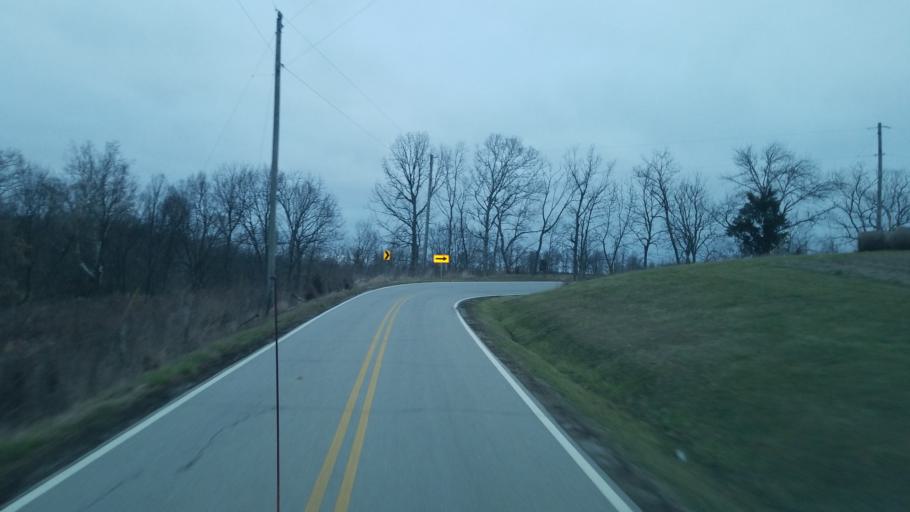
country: US
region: Kentucky
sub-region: Mason County
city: Maysville
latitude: 38.5475
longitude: -83.6985
